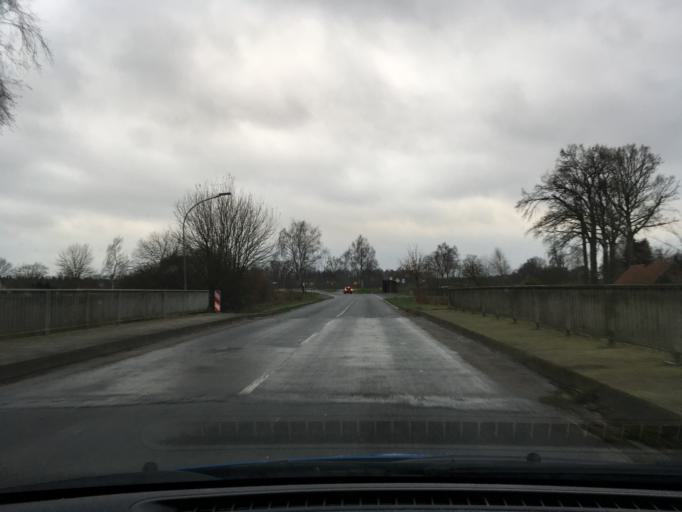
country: DE
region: Lower Saxony
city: Gerdau
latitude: 52.9703
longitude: 10.3924
